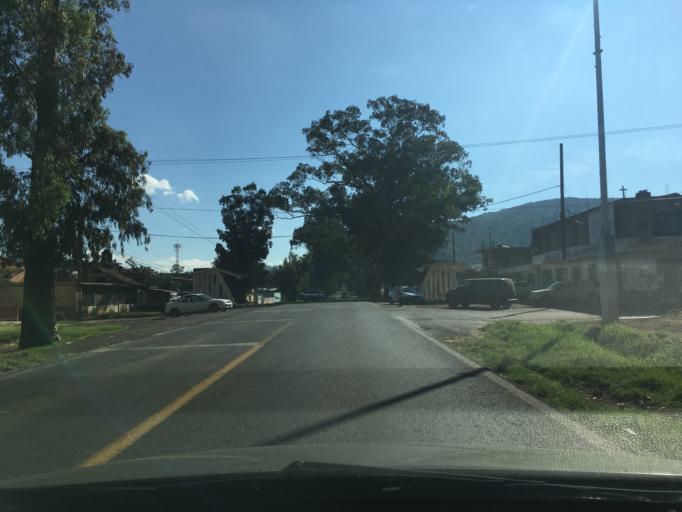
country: MX
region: Mexico
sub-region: Chalco
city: Zopoco
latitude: 19.8436
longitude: -102.0757
